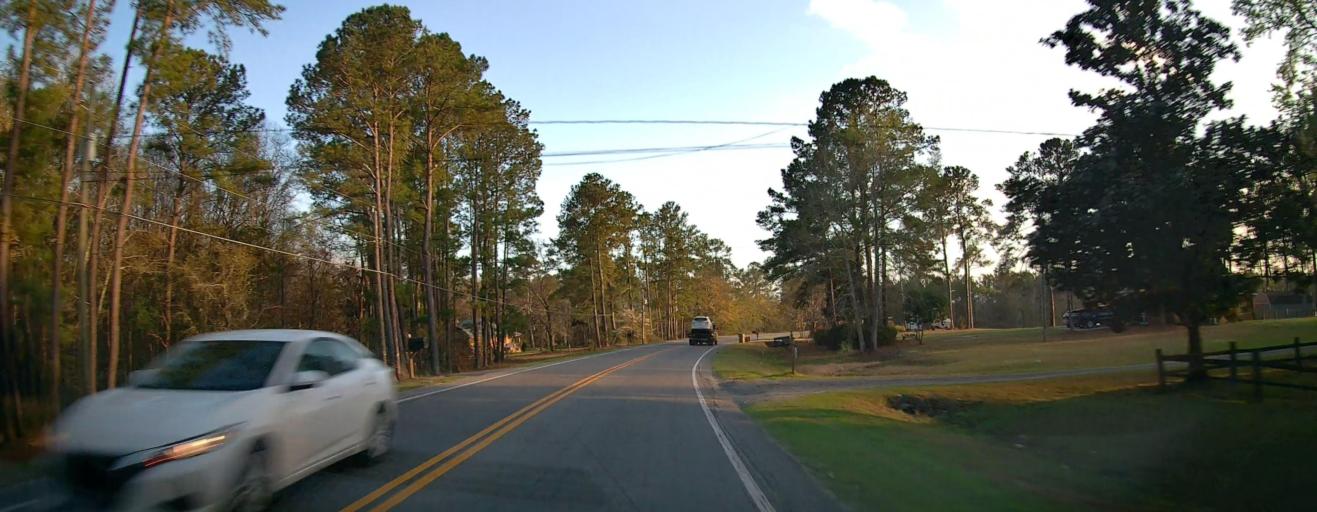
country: US
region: Georgia
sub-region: Chatham County
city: Bloomingdale
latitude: 32.1653
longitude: -81.3851
